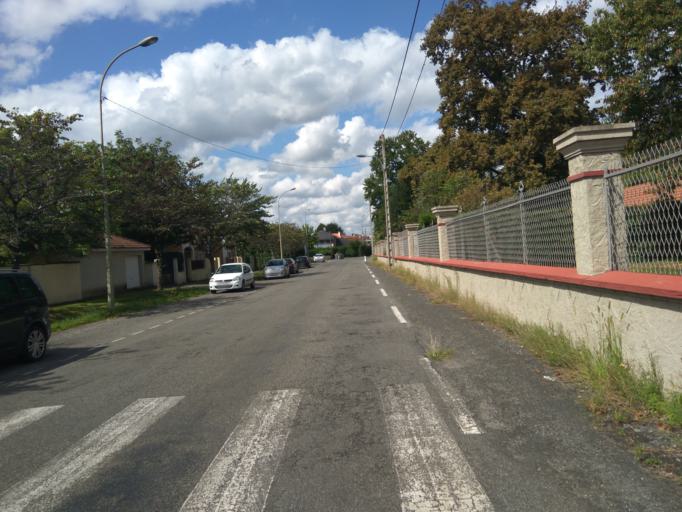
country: FR
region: Aquitaine
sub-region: Departement des Pyrenees-Atlantiques
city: Bizanos
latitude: 43.2998
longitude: -0.3401
